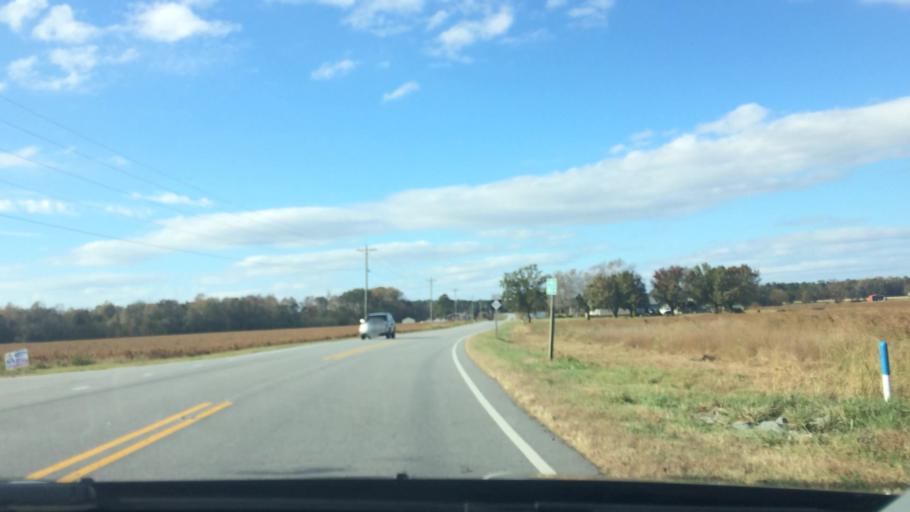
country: US
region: North Carolina
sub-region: Greene County
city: Maury
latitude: 35.4761
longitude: -77.5579
